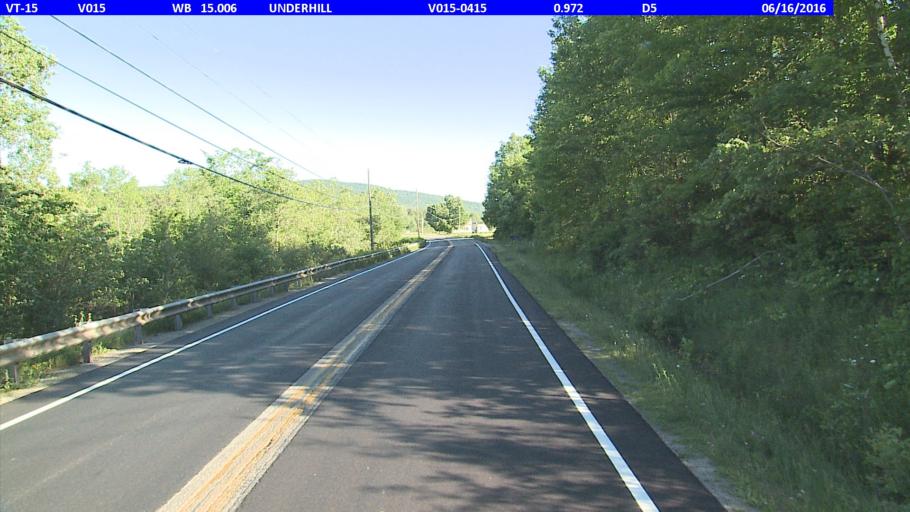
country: US
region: Vermont
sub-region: Chittenden County
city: Jericho
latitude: 44.5384
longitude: -72.9489
